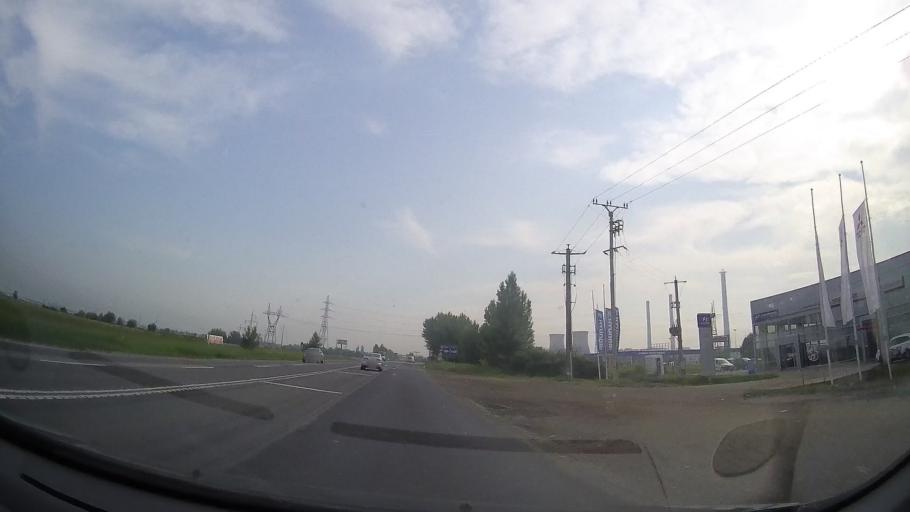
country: RO
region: Timis
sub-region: Comuna Giroc
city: Chisoda
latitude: 45.7038
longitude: 21.1849
